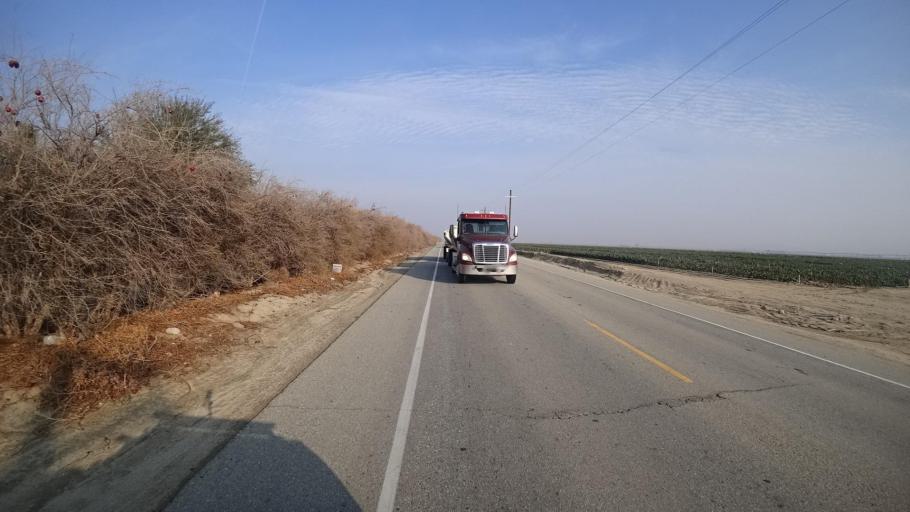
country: US
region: California
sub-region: Kern County
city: Arvin
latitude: 35.0529
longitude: -118.9175
